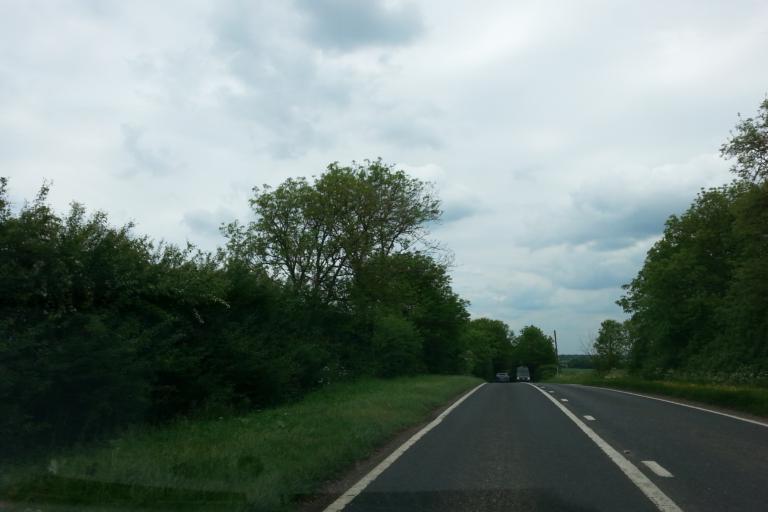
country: GB
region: England
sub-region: Cambridgeshire
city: Ramsey
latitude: 52.4208
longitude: -0.1065
